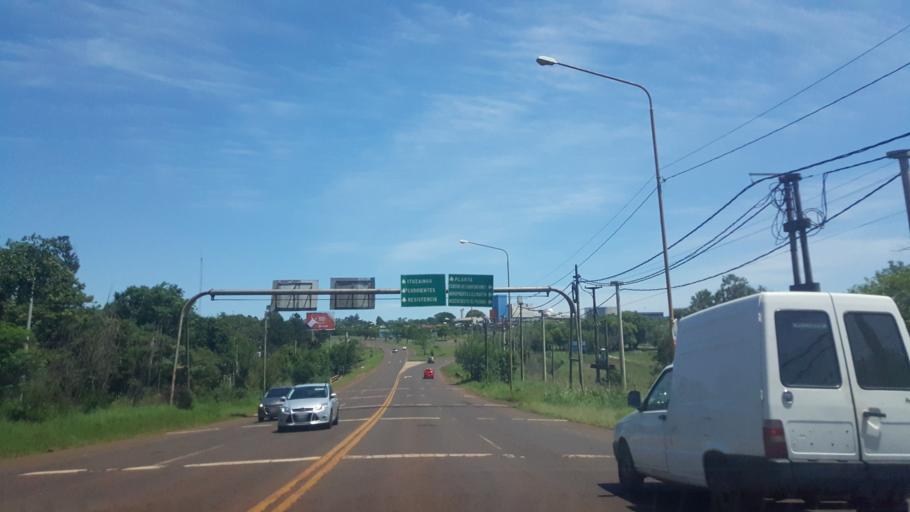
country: AR
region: Misiones
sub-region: Departamento de Capital
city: Posadas
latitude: -27.3986
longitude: -55.9549
